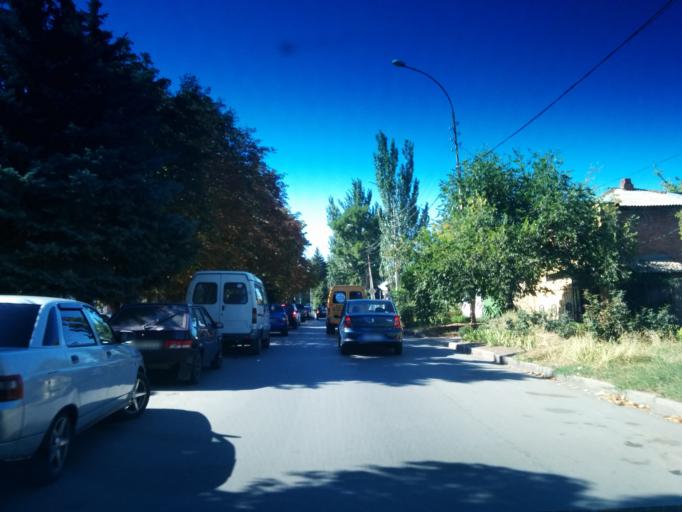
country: RU
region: Rostov
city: Shakhty
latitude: 47.7087
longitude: 40.2207
